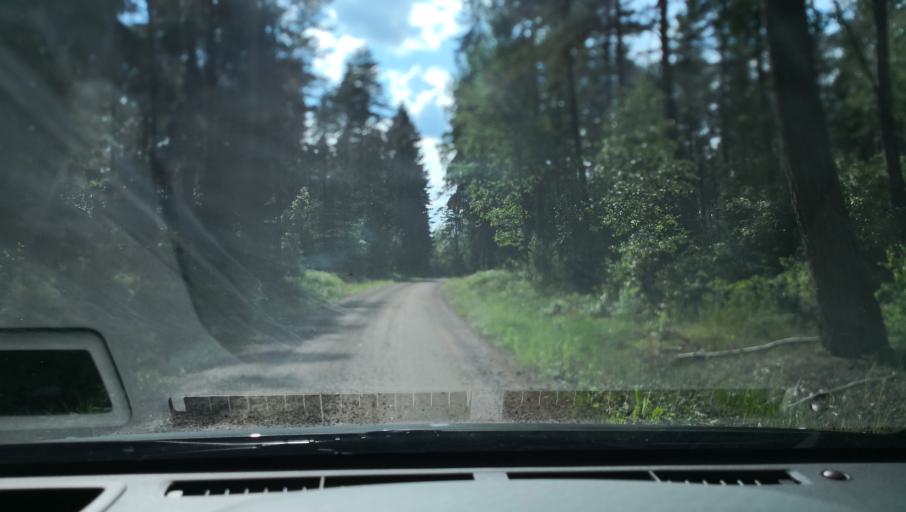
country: SE
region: Uppsala
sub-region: Enkopings Kommun
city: Orsundsbro
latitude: 59.8357
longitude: 17.2527
